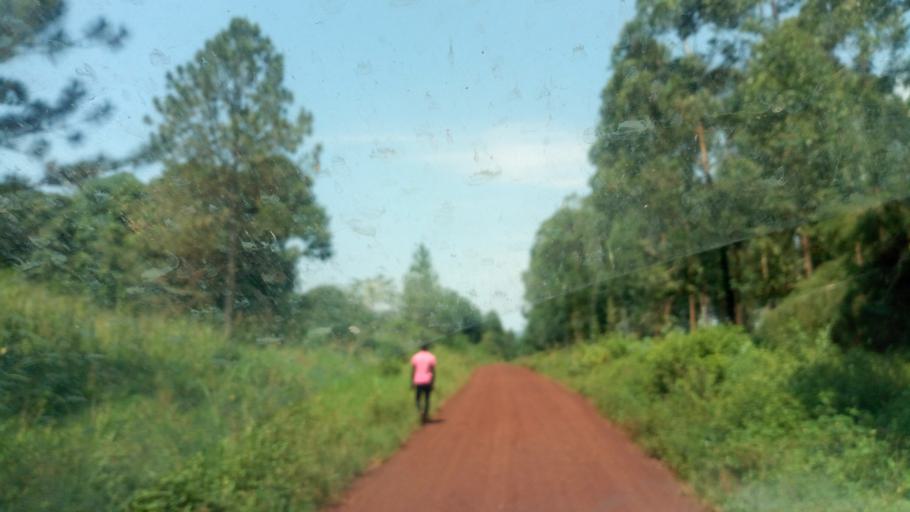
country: UG
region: Western Region
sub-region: Masindi District
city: Masindi
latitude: 1.6668
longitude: 31.8188
